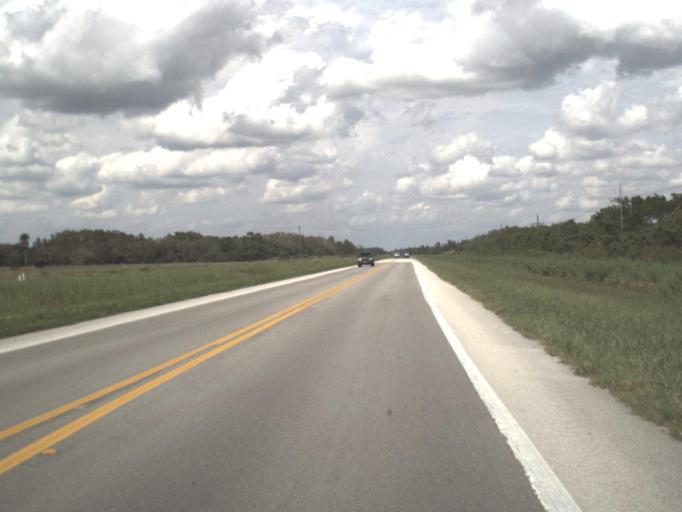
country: US
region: Florida
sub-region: Hendry County
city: Port LaBelle
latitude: 26.6482
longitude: -81.4362
